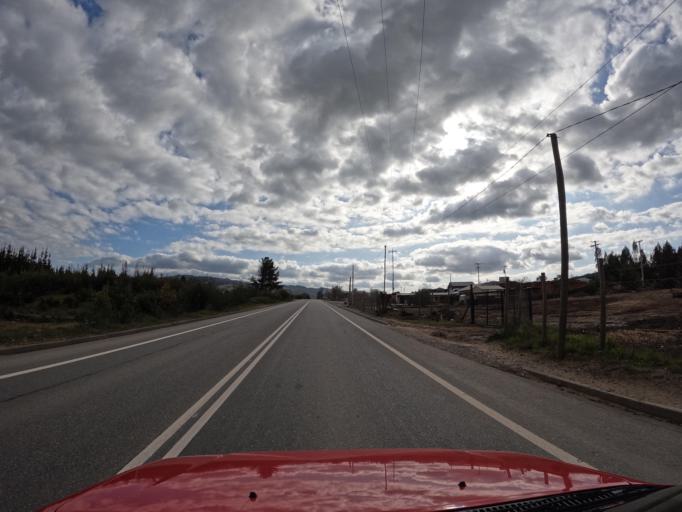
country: CL
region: Maule
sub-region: Provincia de Talca
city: Constitucion
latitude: -35.5564
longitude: -72.1147
